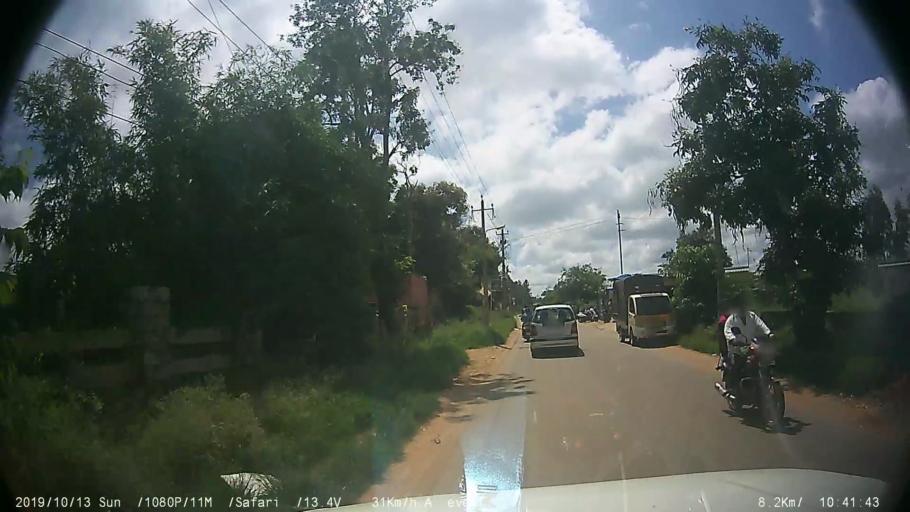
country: IN
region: Karnataka
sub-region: Bangalore Urban
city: Anekal
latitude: 12.8253
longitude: 77.6502
